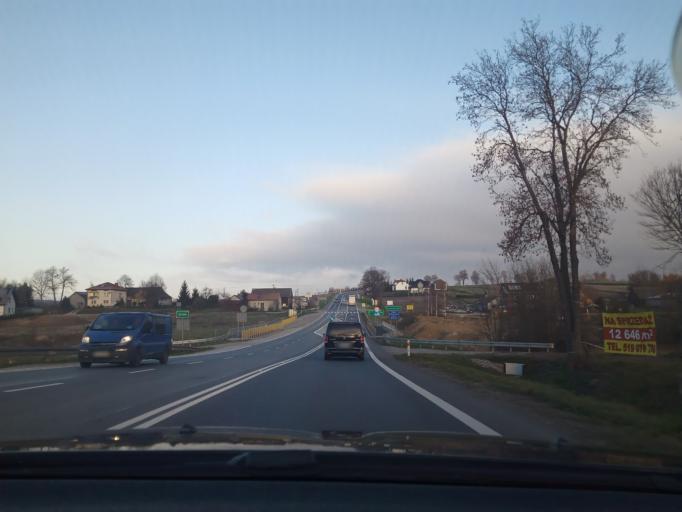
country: PL
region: Lesser Poland Voivodeship
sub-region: Powiat miechowski
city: Miechow
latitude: 50.2931
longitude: 20.0378
